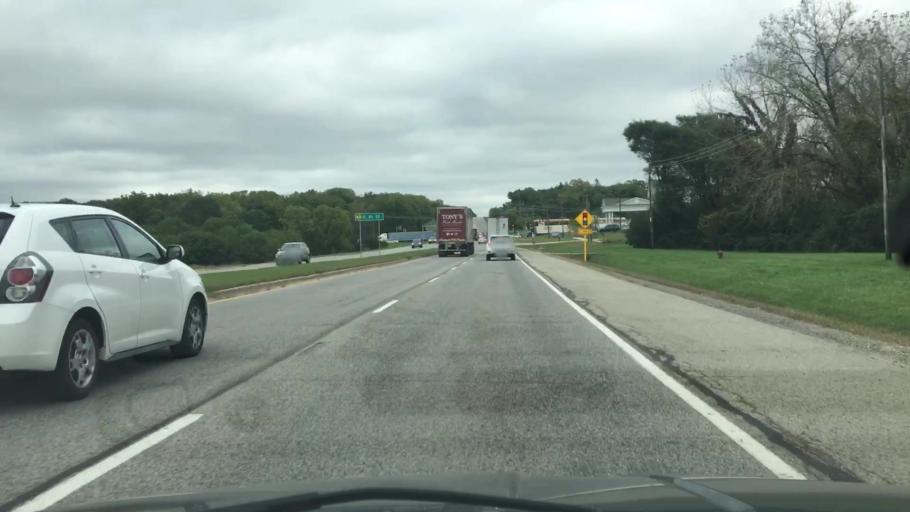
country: US
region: Illinois
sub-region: DuPage County
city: Woodridge
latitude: 41.7497
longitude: -88.0679
